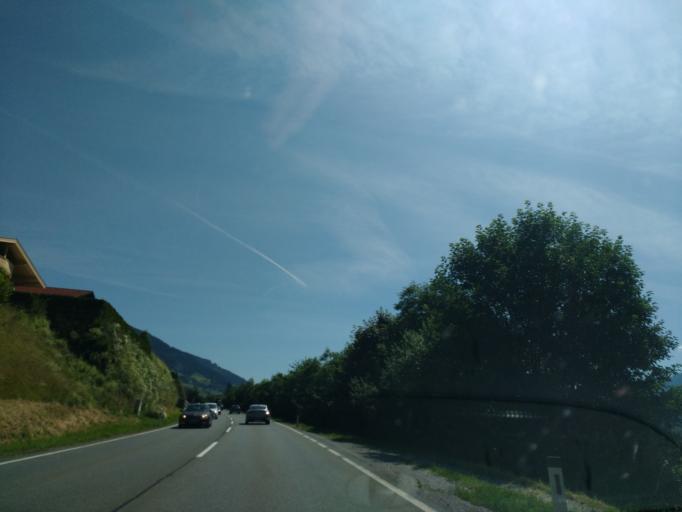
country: AT
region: Salzburg
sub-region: Politischer Bezirk Zell am See
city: Piesendorf
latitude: 47.2872
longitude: 12.6857
